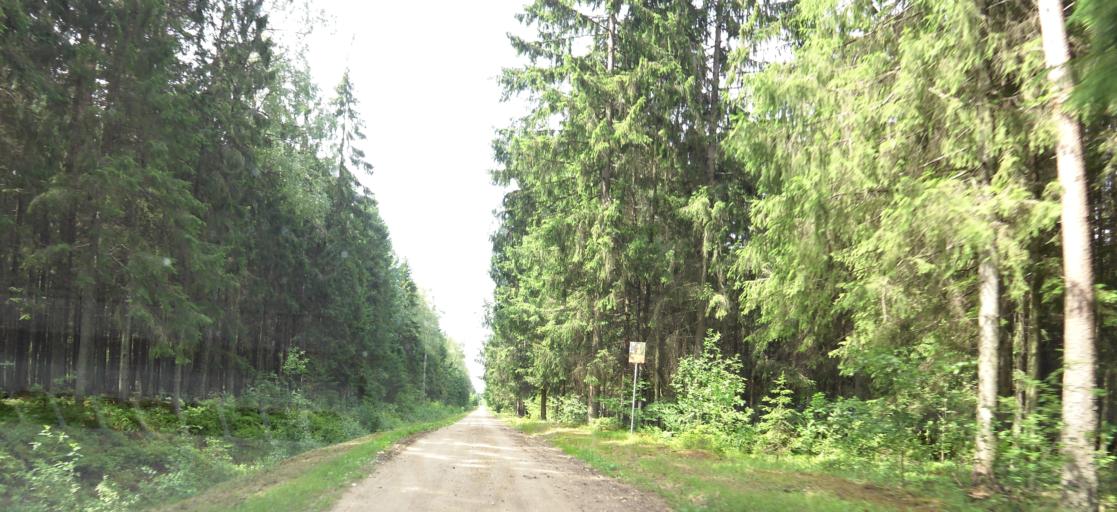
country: LT
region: Panevezys
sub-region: Birzai
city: Birzai
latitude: 56.2709
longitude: 24.7570
